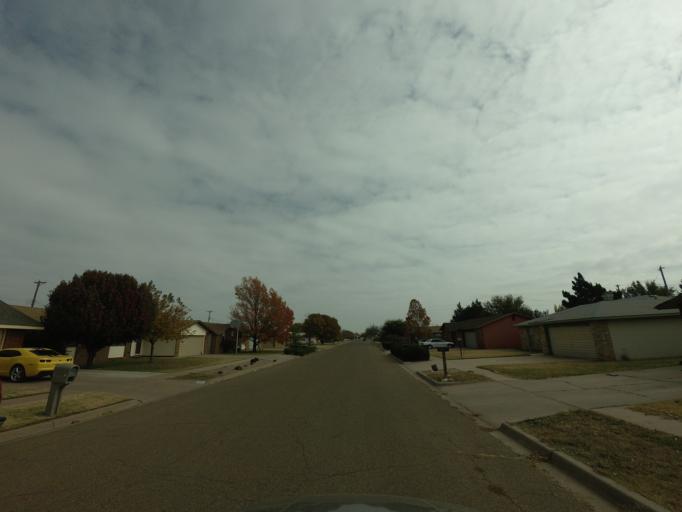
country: US
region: New Mexico
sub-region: Curry County
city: Clovis
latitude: 34.4299
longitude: -103.2294
